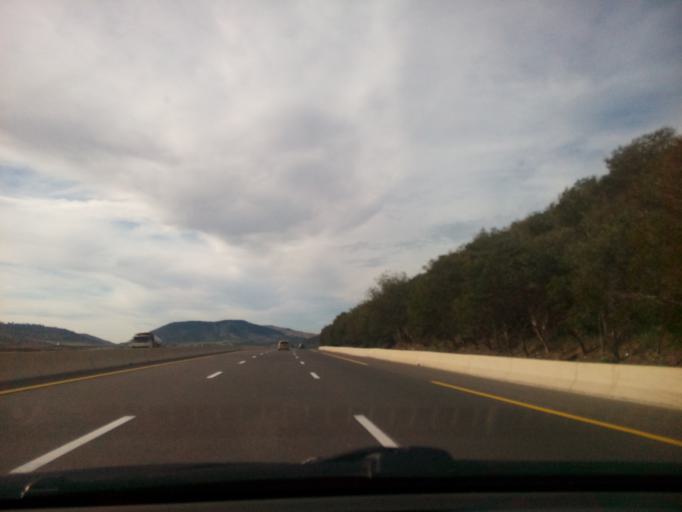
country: DZ
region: Sidi Bel Abbes
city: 'Ain el Berd
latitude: 35.4294
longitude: -0.4606
